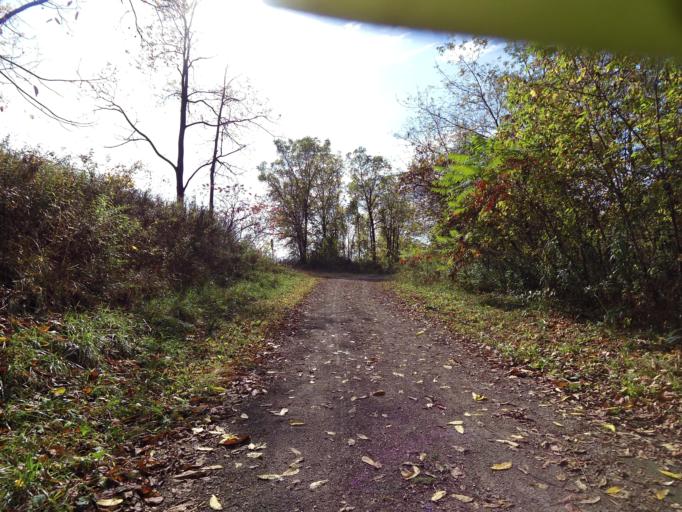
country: CA
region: Ontario
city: Brantford
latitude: 43.1585
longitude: -80.1825
